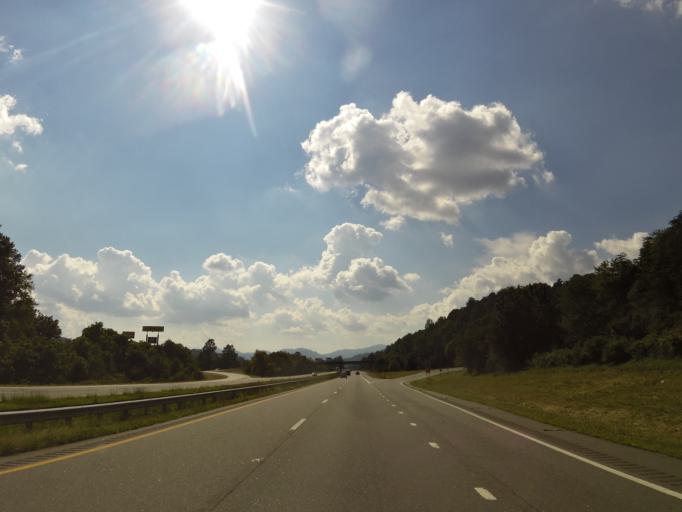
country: US
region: North Carolina
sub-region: McDowell County
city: West Marion
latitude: 35.6391
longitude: -82.1407
